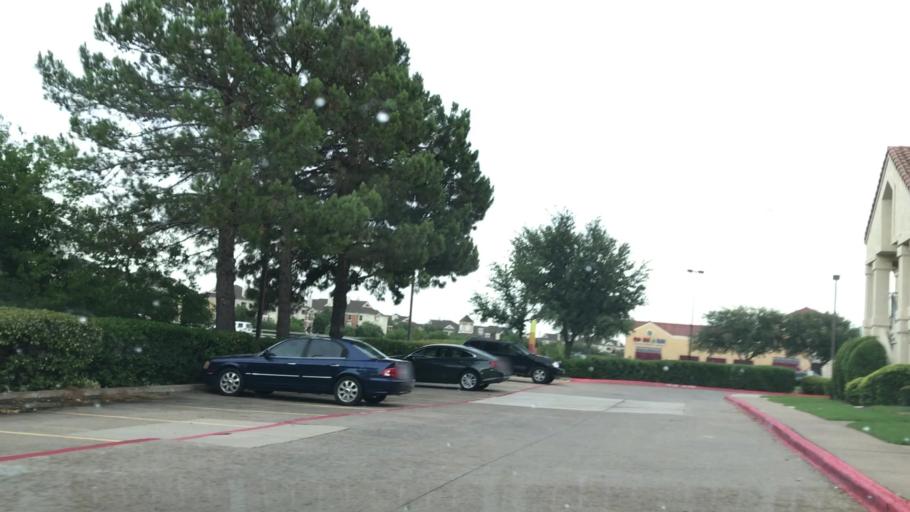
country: US
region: Texas
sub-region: Dallas County
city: Farmers Branch
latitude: 32.8934
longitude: -96.9613
